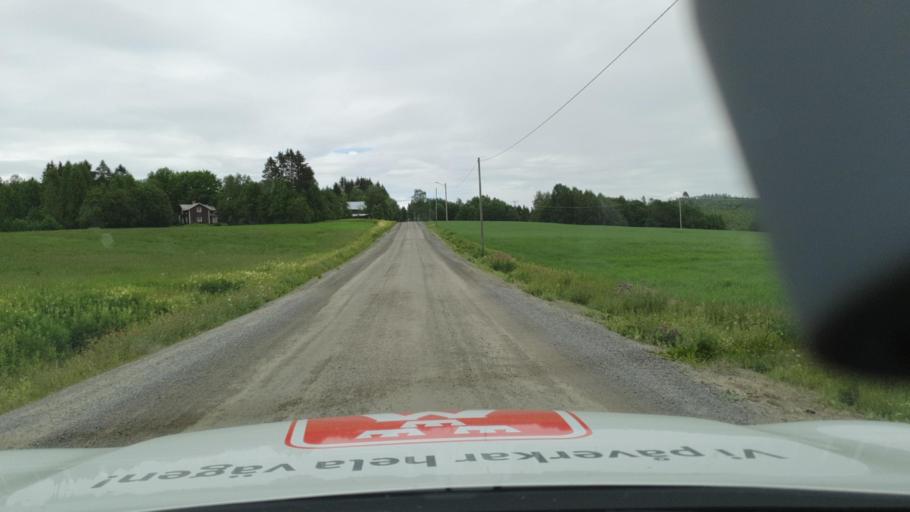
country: SE
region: Vaesterbotten
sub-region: Nordmalings Kommun
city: Nordmaling
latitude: 63.6464
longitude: 19.4290
